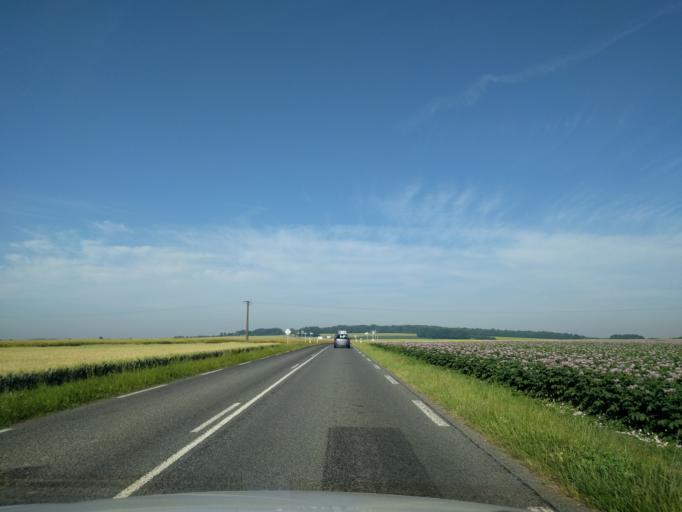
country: FR
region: Picardie
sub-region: Departement de la Somme
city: Montdidier
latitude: 49.6372
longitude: 2.4809
